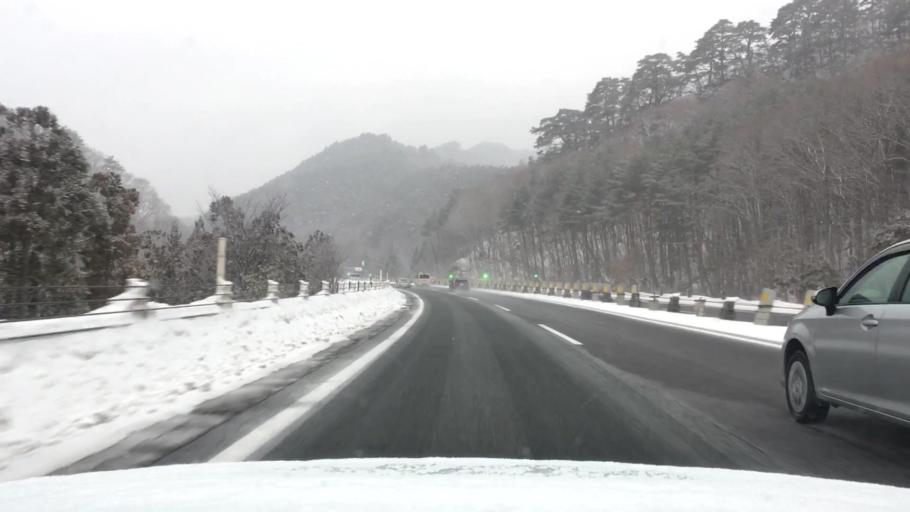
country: JP
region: Akita
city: Hanawa
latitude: 40.1155
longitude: 141.0314
